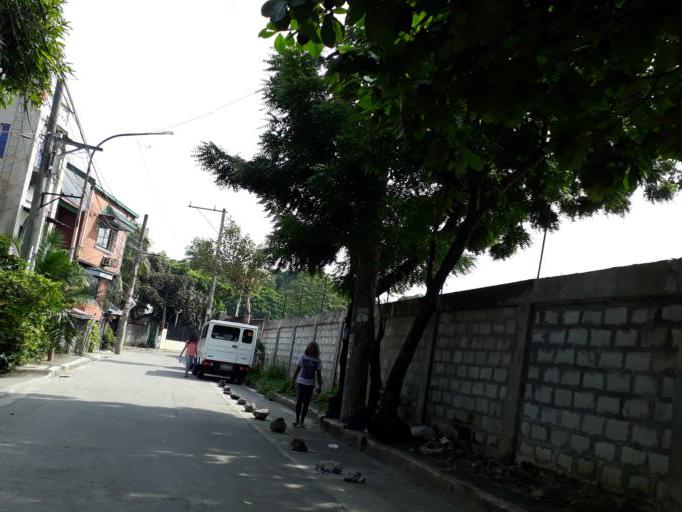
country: PH
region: Calabarzon
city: Del Monte
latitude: 14.6640
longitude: 121.0020
